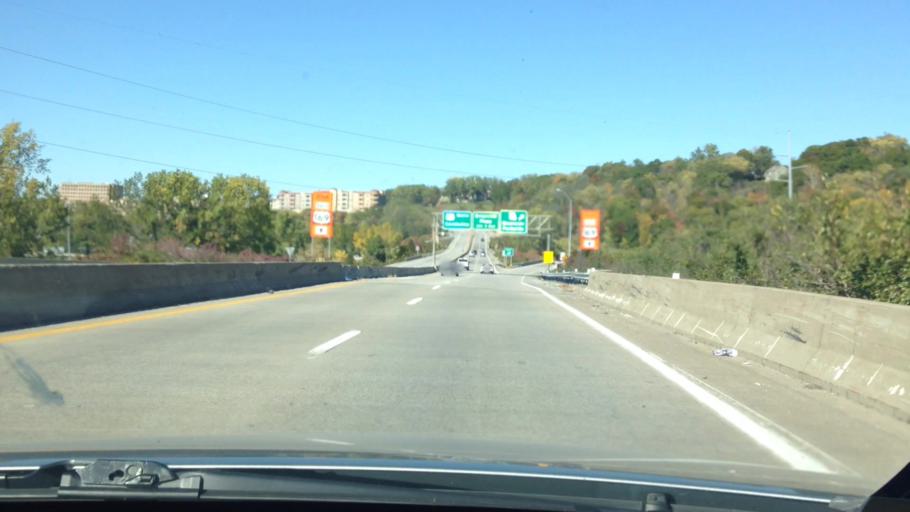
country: US
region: Missouri
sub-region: Platte County
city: Riverside
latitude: 39.1563
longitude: -94.5885
